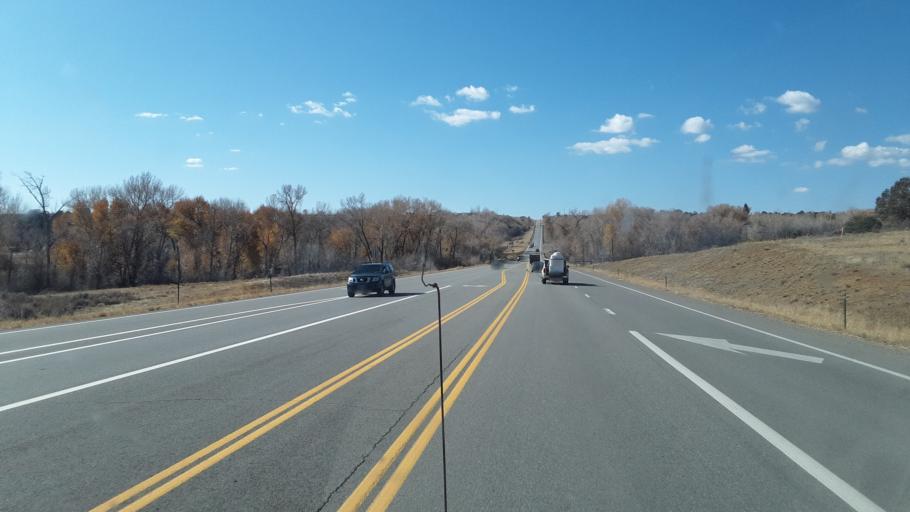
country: US
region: Colorado
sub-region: La Plata County
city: Durango
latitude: 37.2293
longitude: -107.7504
